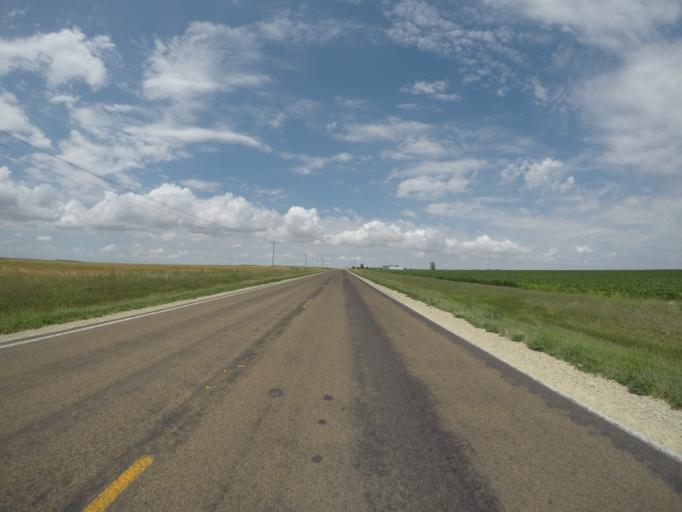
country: US
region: Kansas
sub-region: Rawlins County
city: Atwood
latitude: 39.8399
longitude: -101.0468
